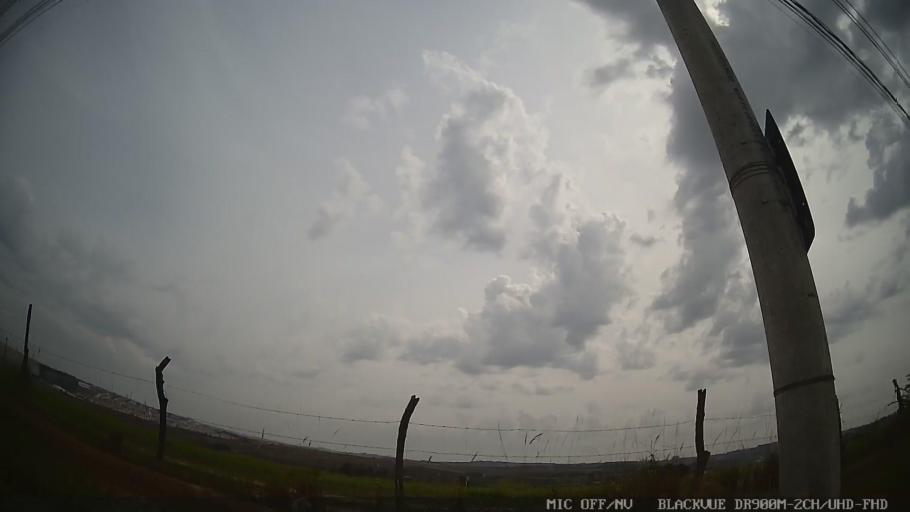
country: BR
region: Sao Paulo
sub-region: Indaiatuba
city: Indaiatuba
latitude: -23.1019
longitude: -47.2573
